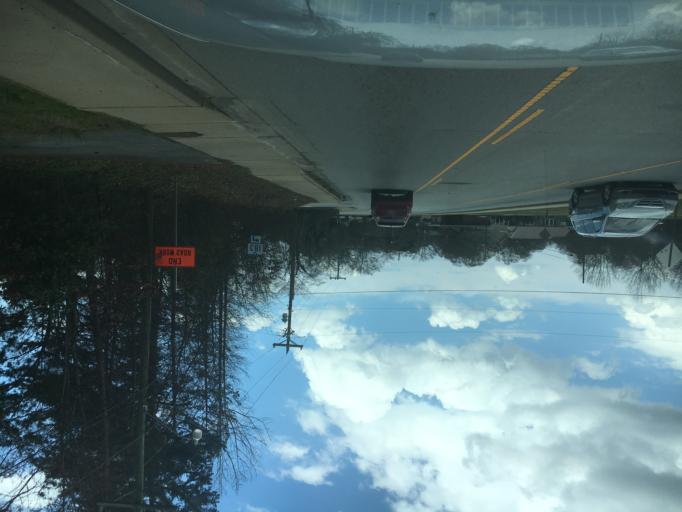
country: US
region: South Carolina
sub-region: Oconee County
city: Westminster
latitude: 34.6698
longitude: -83.1032
